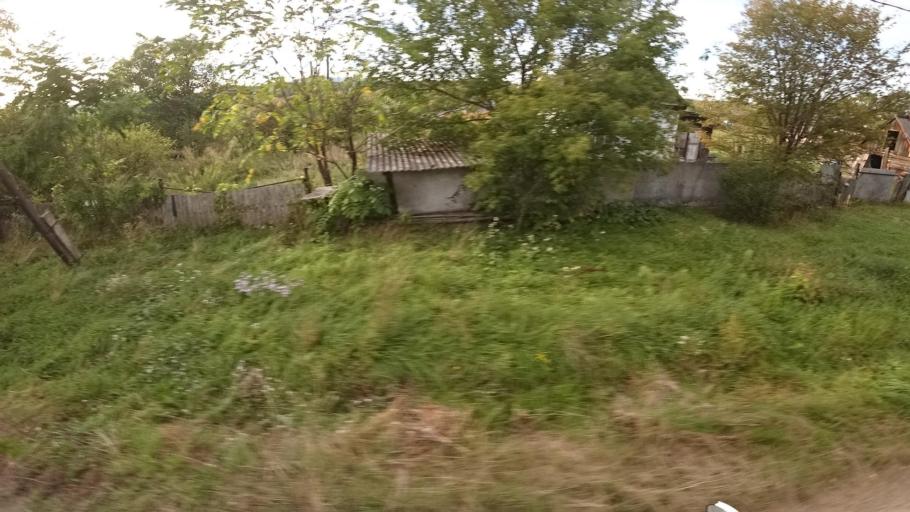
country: RU
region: Primorskiy
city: Yakovlevka
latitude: 44.4185
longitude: 133.4499
